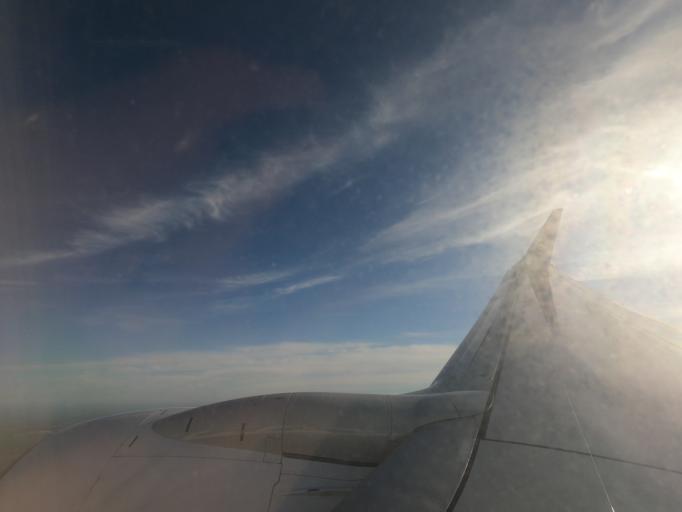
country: GB
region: England
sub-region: Suffolk
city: Kedington
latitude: 52.0271
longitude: 0.4936
